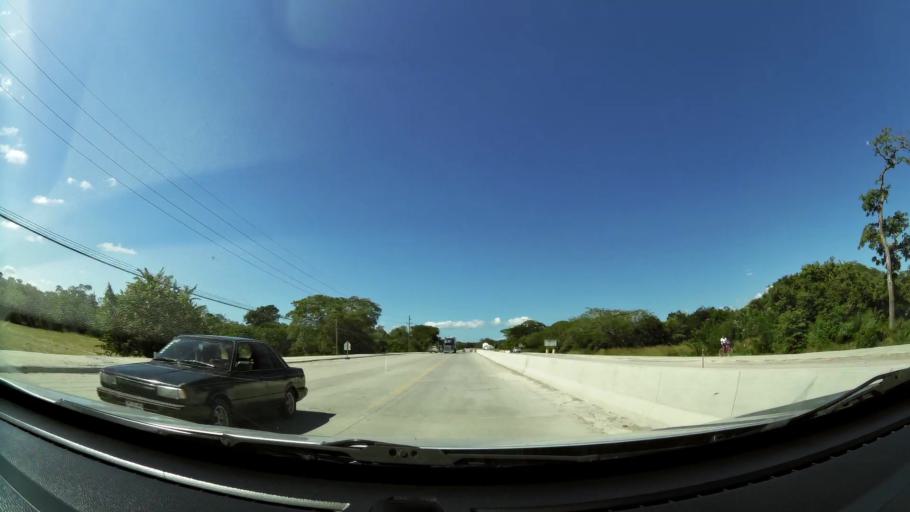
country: CR
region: Guanacaste
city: Bagaces
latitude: 10.5452
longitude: -85.3527
